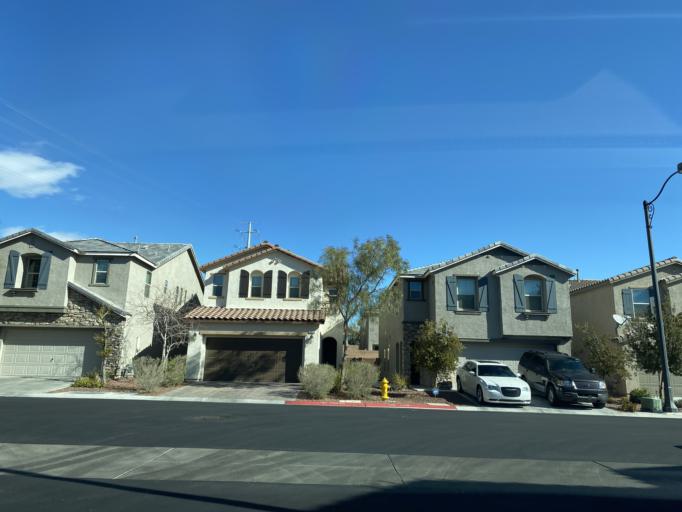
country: US
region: Nevada
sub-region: Clark County
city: Summerlin South
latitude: 36.3050
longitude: -115.3331
